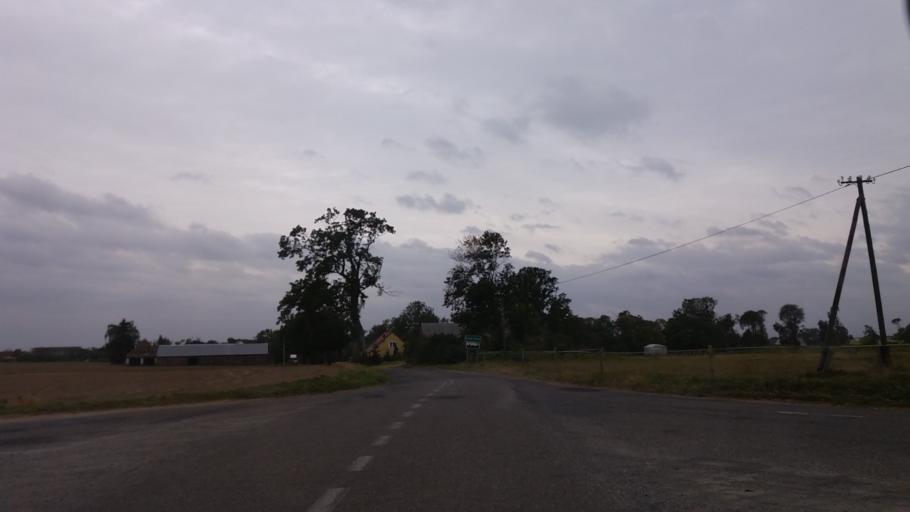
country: PL
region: Lubusz
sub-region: Powiat strzelecko-drezdenecki
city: Strzelce Krajenskie
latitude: 52.9332
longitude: 15.5613
